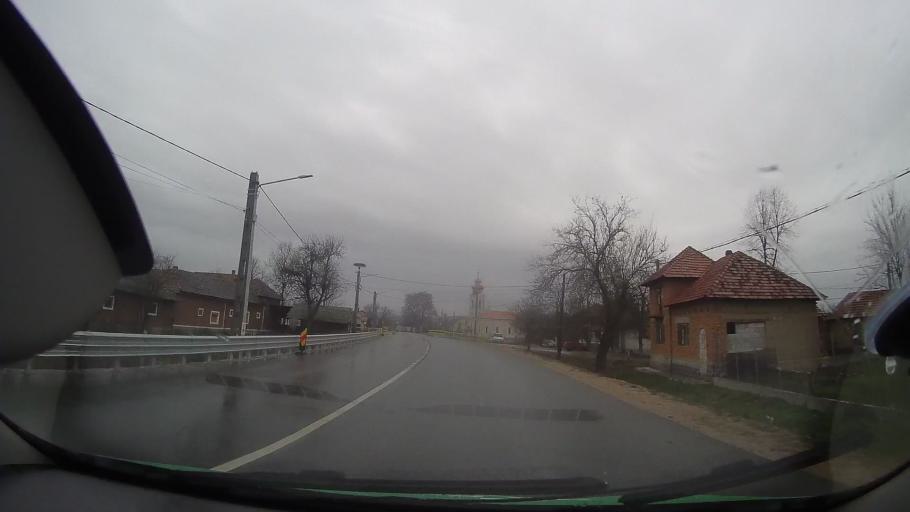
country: RO
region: Bihor
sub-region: Comuna Pocola
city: Pocola
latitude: 46.6938
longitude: 22.2948
